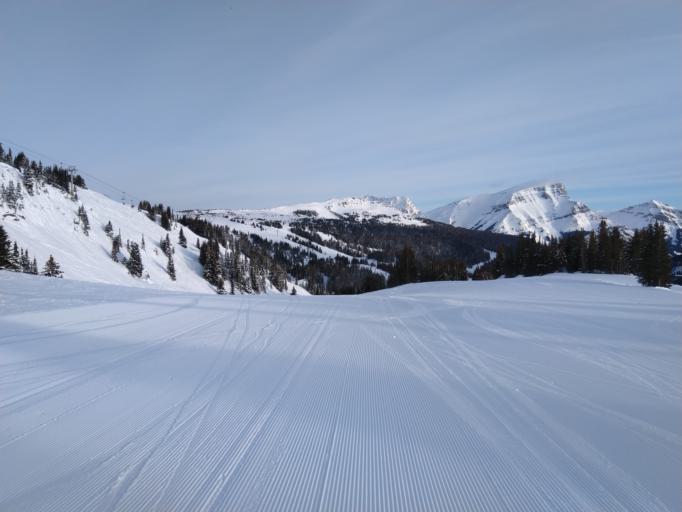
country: CA
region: Alberta
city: Banff
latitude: 51.0721
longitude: -115.7828
